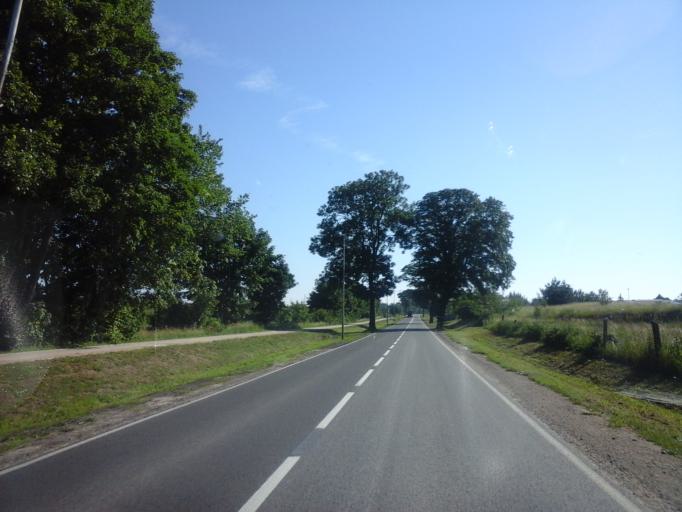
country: PL
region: West Pomeranian Voivodeship
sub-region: Powiat drawski
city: Drawsko Pomorskie
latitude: 53.5193
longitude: 15.7801
